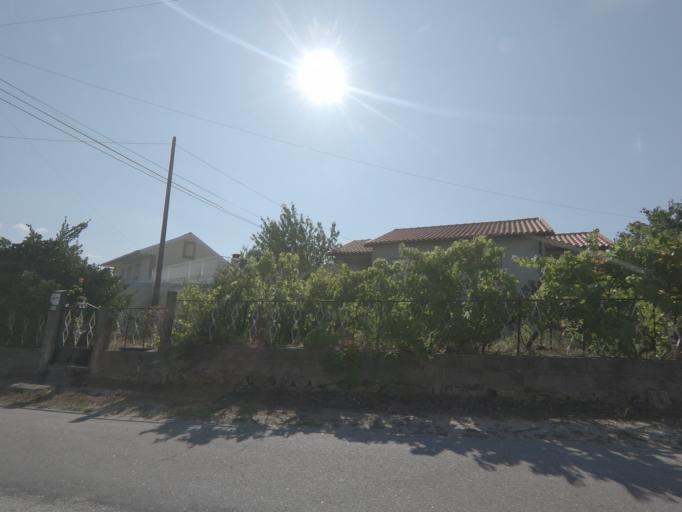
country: PT
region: Viseu
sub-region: Moimenta da Beira
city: Moimenta da Beira
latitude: 40.9910
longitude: -7.5619
